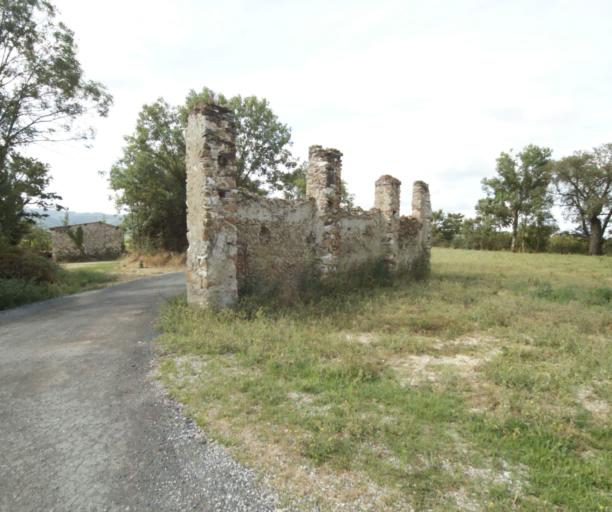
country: FR
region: Midi-Pyrenees
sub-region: Departement du Tarn
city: Soreze
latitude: 43.4875
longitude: 2.0875
